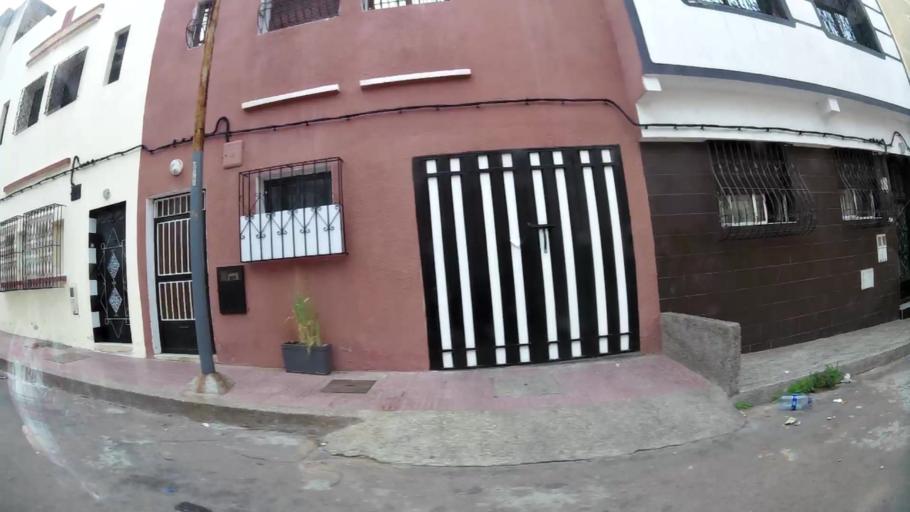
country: MA
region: Grand Casablanca
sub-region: Casablanca
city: Casablanca
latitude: 33.5314
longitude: -7.6095
